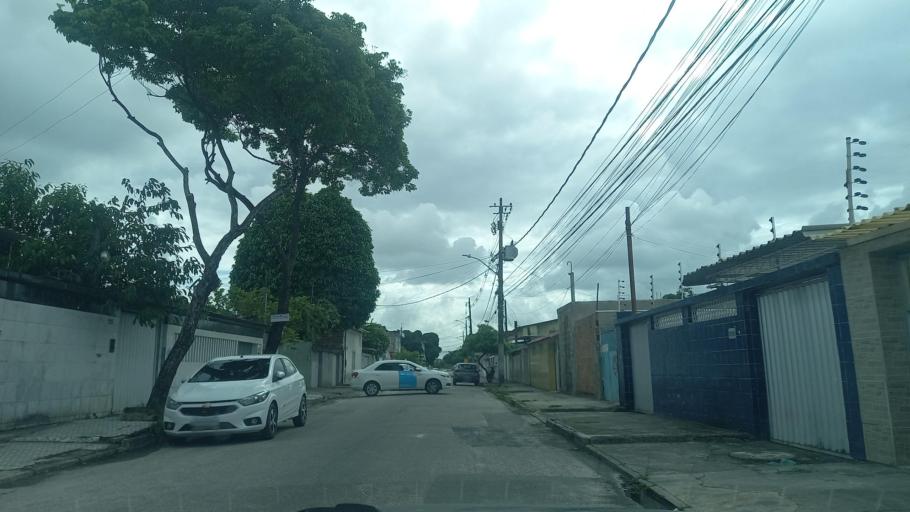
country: BR
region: Pernambuco
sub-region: Recife
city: Recife
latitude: -8.1086
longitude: -34.9177
